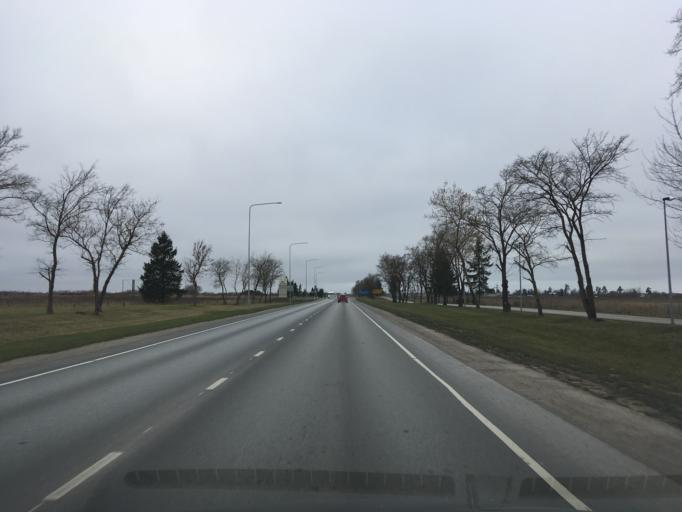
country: EE
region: Ida-Virumaa
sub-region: Narva linn
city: Narva
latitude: 59.3859
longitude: 28.1516
